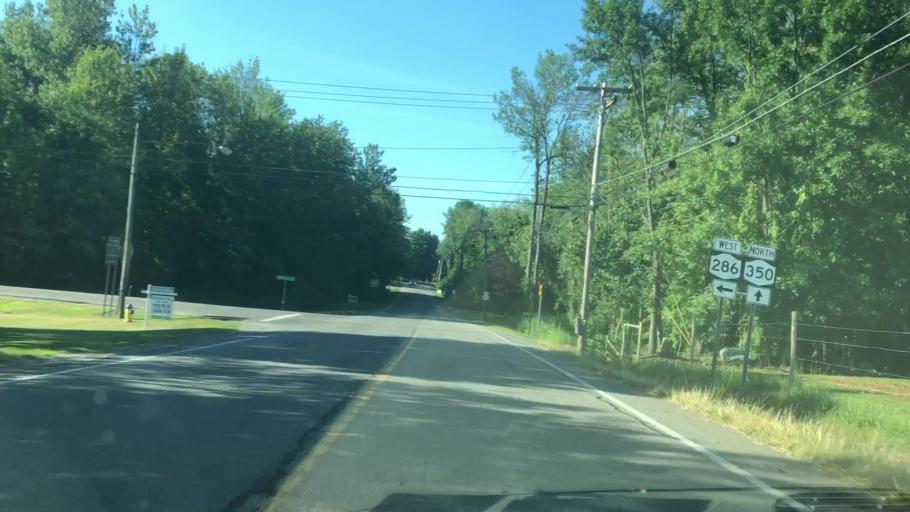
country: US
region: New York
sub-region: Wayne County
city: Ontario
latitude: 43.1641
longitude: -77.2899
